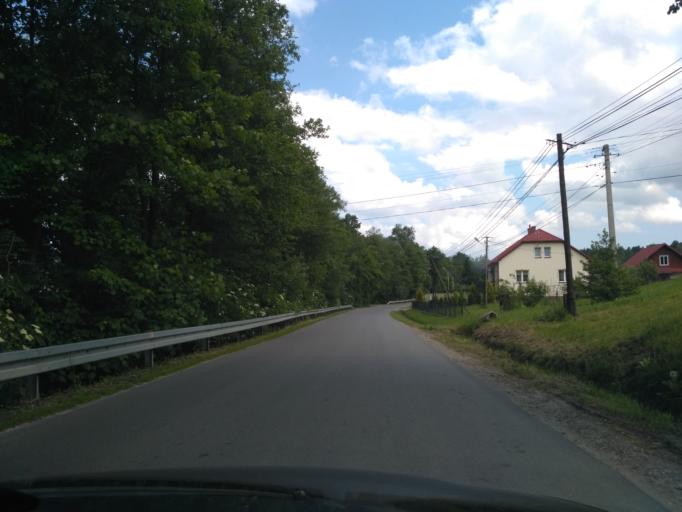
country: PL
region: Subcarpathian Voivodeship
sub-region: Powiat rzeszowski
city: Blazowa
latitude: 49.8666
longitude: 22.0673
